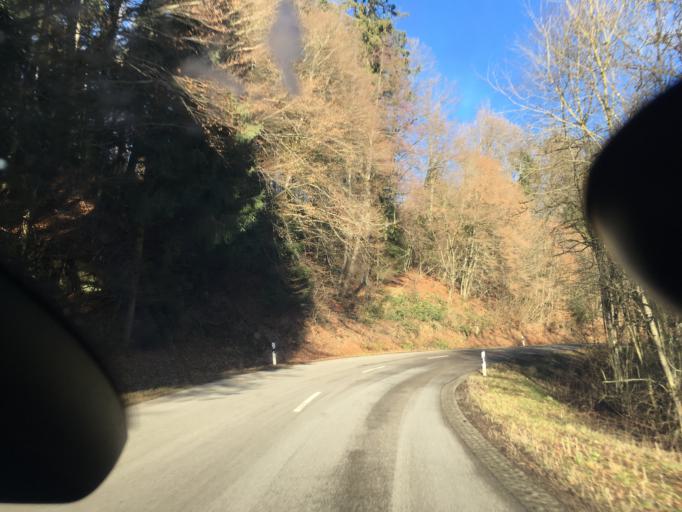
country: DE
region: Baden-Wuerttemberg
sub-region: Freiburg Region
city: Gorwihl
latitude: 47.6390
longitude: 8.1156
